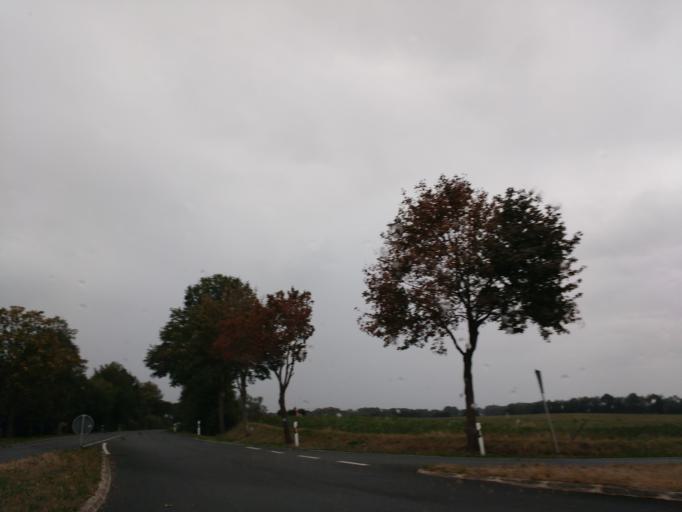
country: DE
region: North Rhine-Westphalia
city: Rietberg
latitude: 51.7461
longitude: 8.4488
